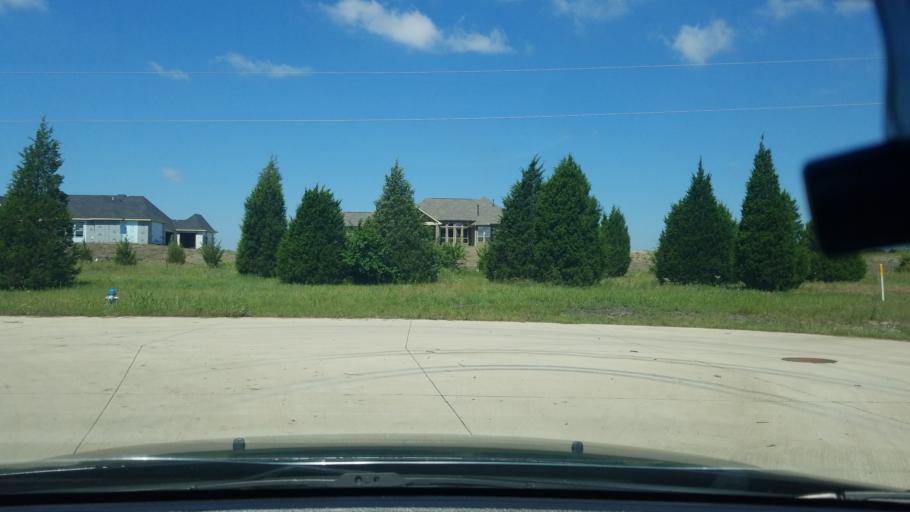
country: US
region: Texas
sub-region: Dallas County
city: Sunnyvale
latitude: 32.8013
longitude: -96.5727
